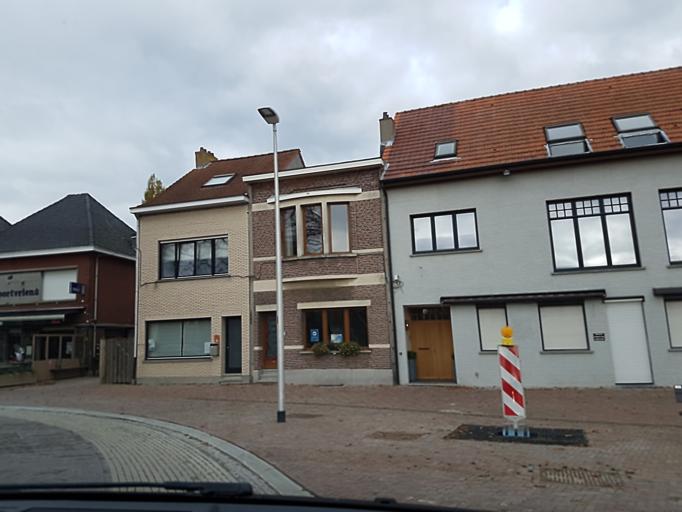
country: BE
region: Flanders
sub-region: Provincie Antwerpen
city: Wommelgem
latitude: 51.1755
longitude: 4.5243
